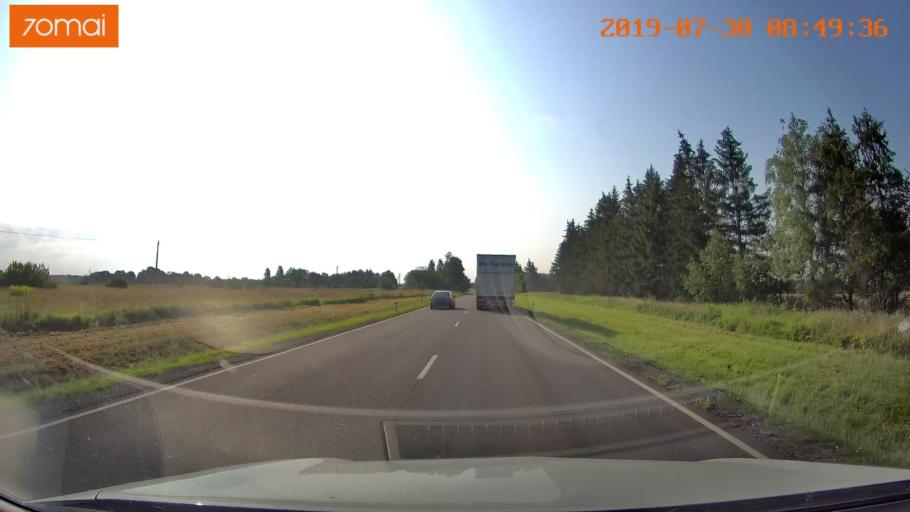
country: RU
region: Kaliningrad
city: Chernyakhovsk
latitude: 54.6124
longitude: 21.9249
